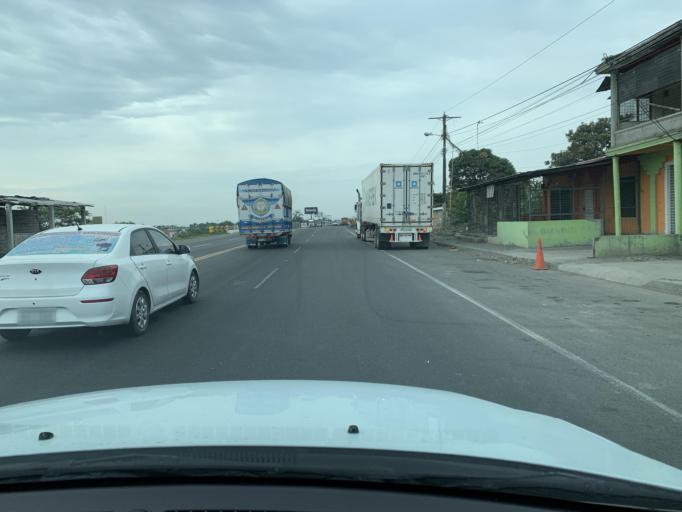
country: EC
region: Guayas
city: Yaguachi Nuevo
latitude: -2.2460
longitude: -79.6360
